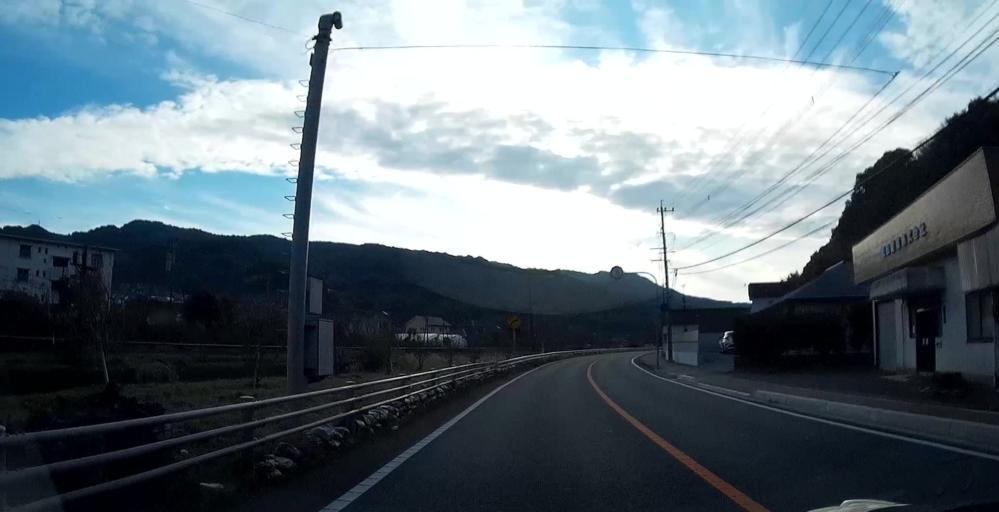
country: JP
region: Kumamoto
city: Uto
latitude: 32.6694
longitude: 130.5510
